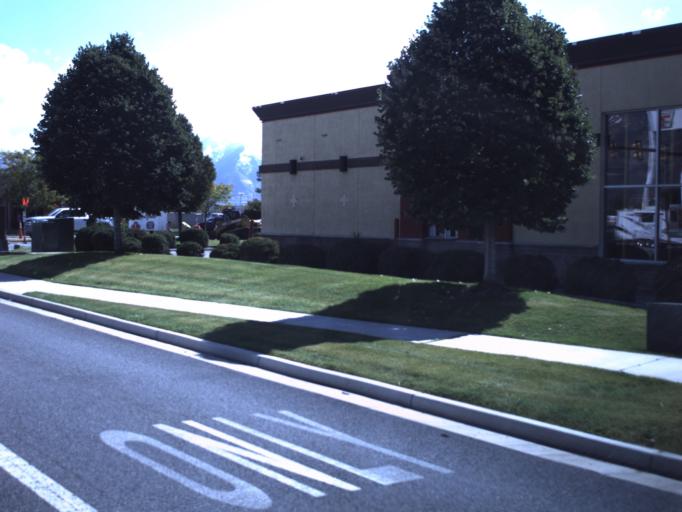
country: US
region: Utah
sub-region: Utah County
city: Springville
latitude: 40.1613
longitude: -111.6431
